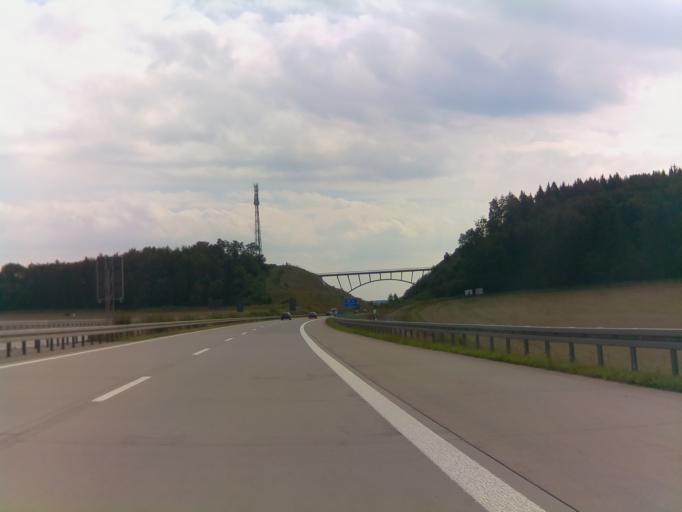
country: DE
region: Thuringia
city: Wolfershausen
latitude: 50.4615
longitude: 10.4531
